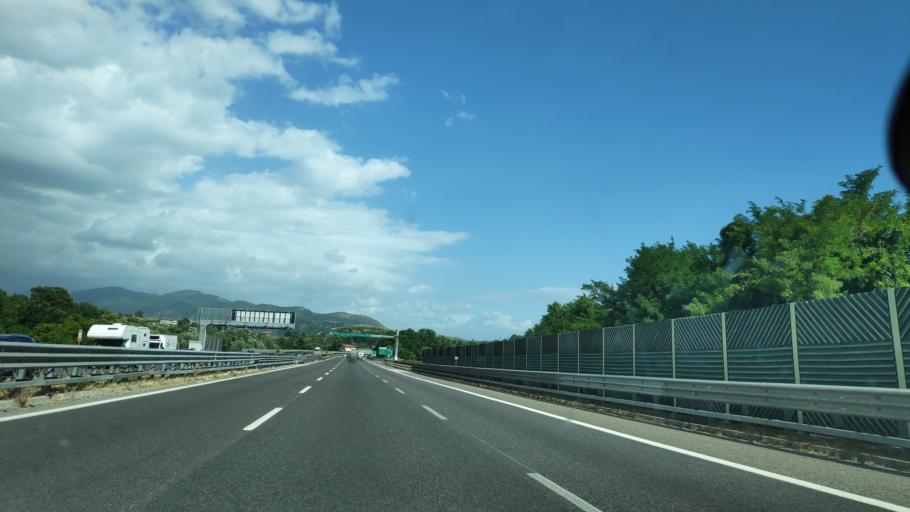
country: IT
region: Campania
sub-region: Provincia di Salerno
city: San Mango Piemonte
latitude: 40.6871
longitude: 14.8456
